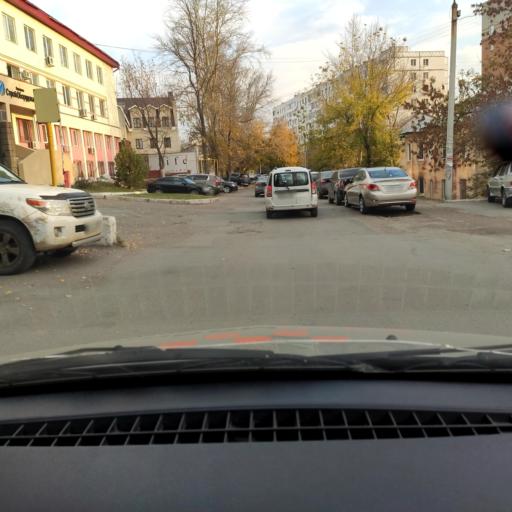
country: RU
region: Bashkortostan
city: Ufa
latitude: 54.7376
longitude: 55.9957
